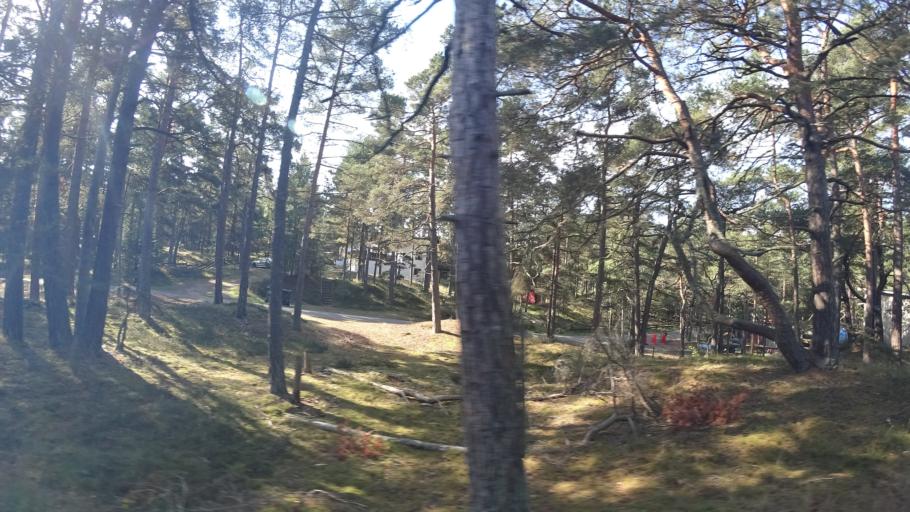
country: SE
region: Skane
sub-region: Kristianstads Kommun
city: Ahus
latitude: 55.9179
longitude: 14.3065
